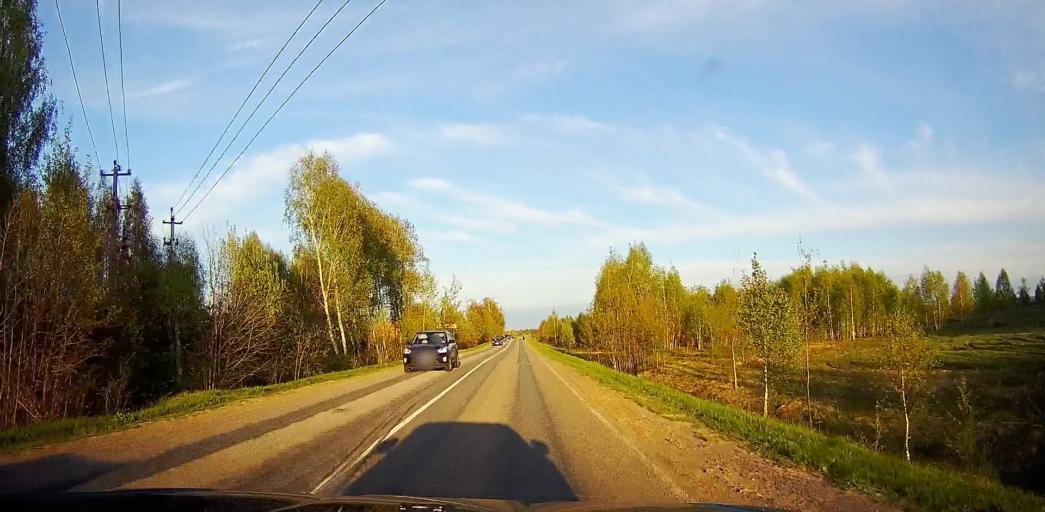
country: RU
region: Moskovskaya
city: Meshcherino
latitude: 55.2507
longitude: 38.2850
